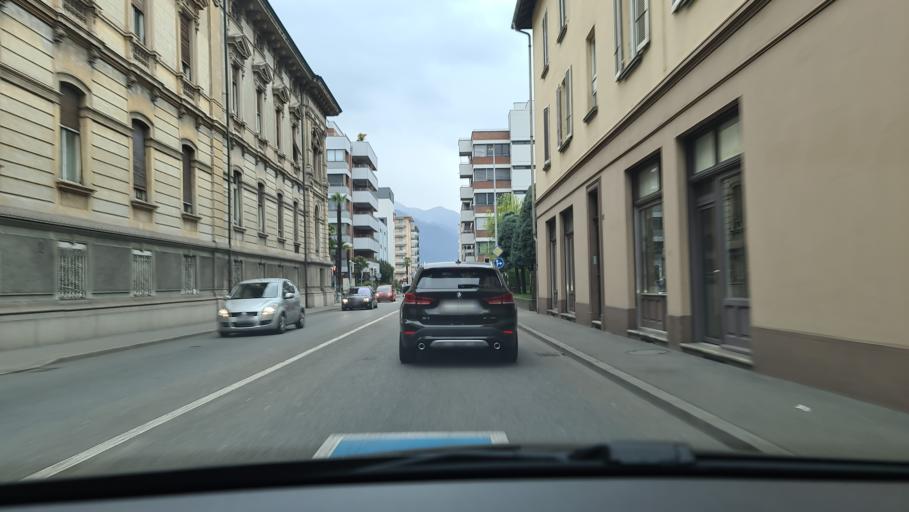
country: CH
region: Ticino
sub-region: Locarno District
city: Locarno
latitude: 46.1677
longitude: 8.7978
